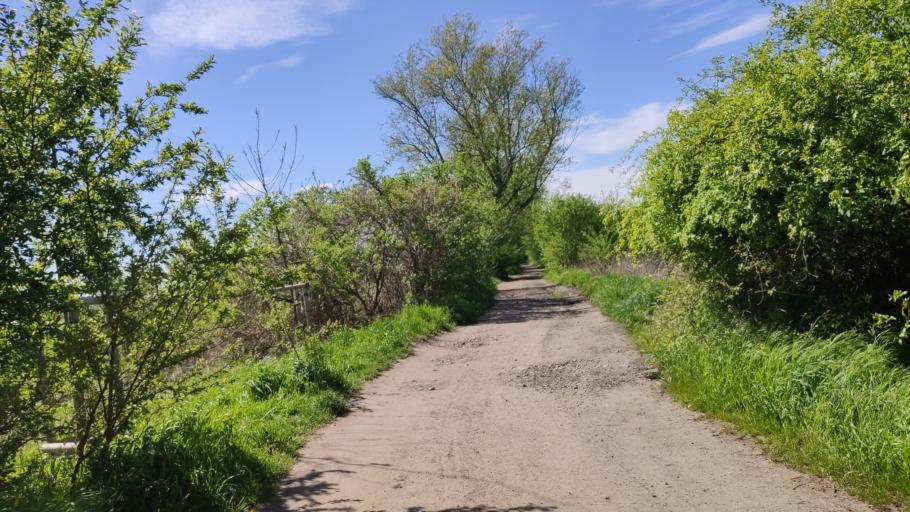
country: PL
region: Lower Silesian Voivodeship
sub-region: Powiat wroclawski
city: Zerniki Wroclawskie
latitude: 51.0597
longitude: 17.0453
